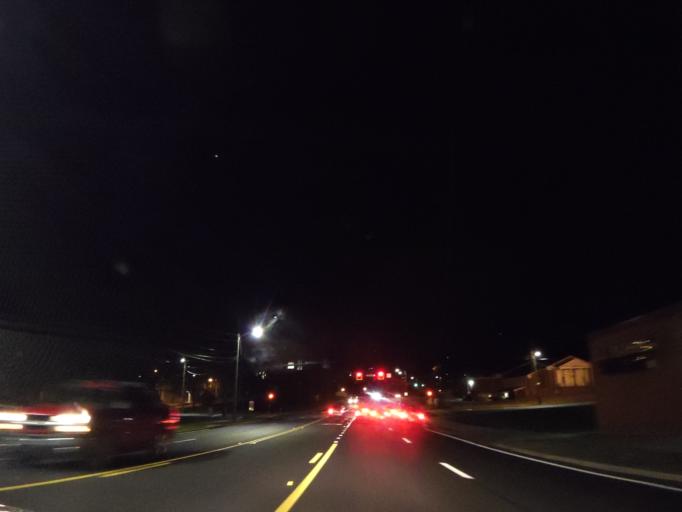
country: US
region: Georgia
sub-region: Whitfield County
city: Dalton
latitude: 34.7743
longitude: -84.9709
